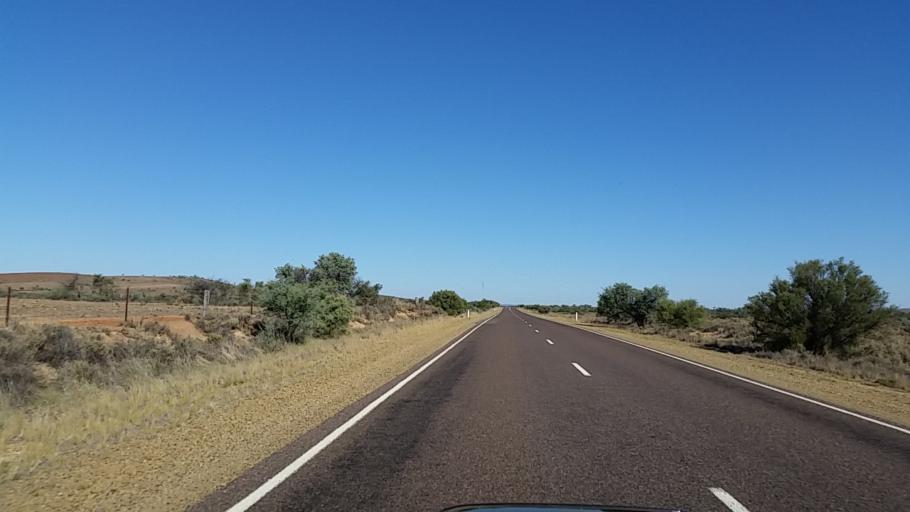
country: AU
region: South Australia
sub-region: Flinders Ranges
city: Quorn
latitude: -32.3447
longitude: 138.4852
